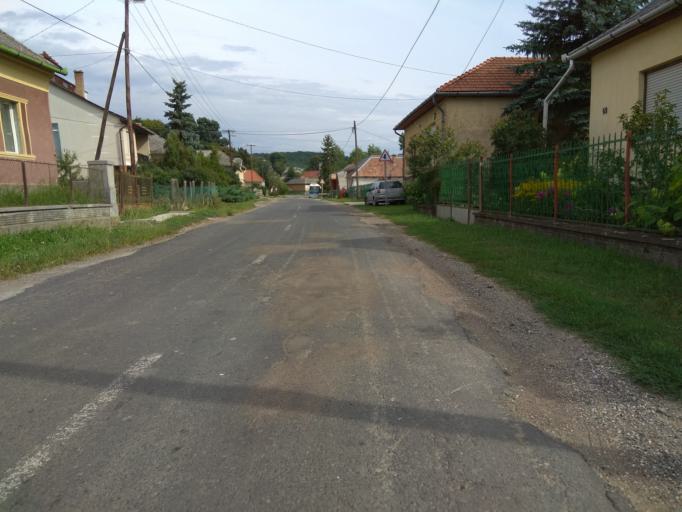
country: HU
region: Heves
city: Tarnalelesz
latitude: 48.0277
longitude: 20.2576
